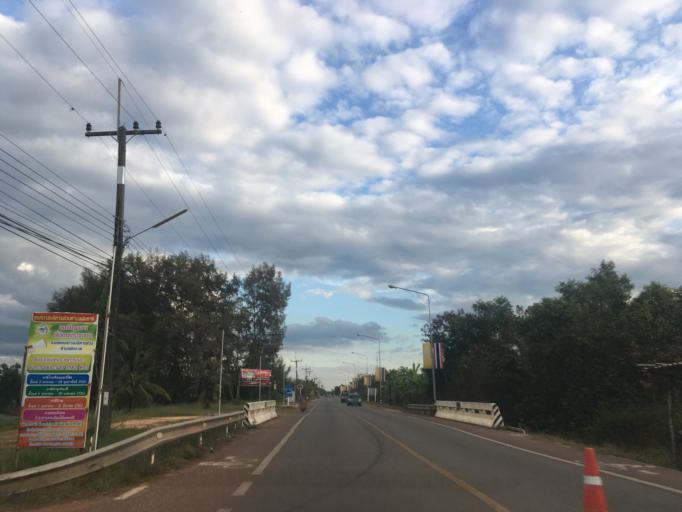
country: TH
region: Chanthaburi
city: Na Yai Am
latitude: 12.7155
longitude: 101.7694
